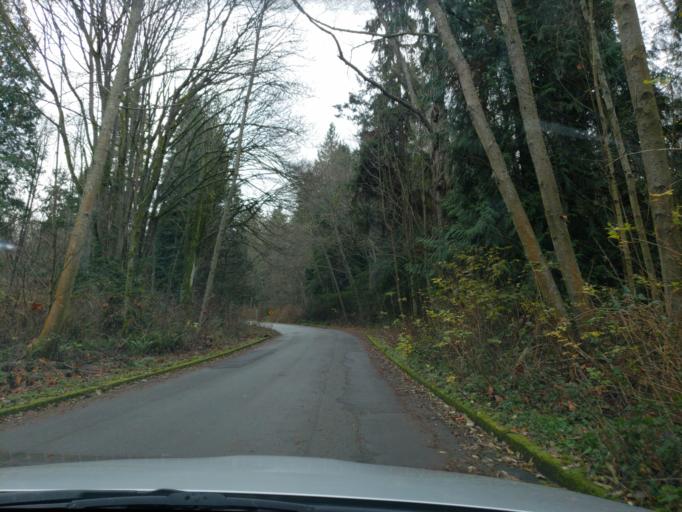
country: US
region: Washington
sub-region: King County
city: Seattle
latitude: 47.6639
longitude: -122.4111
